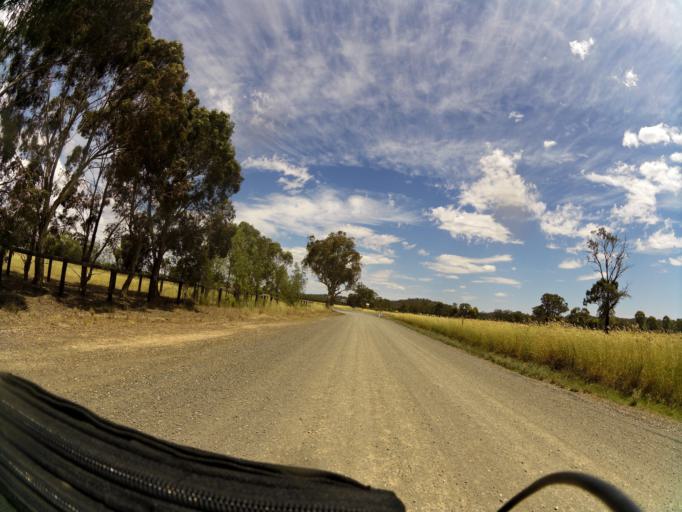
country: AU
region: Victoria
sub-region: Campaspe
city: Kyabram
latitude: -36.7580
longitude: 145.1021
